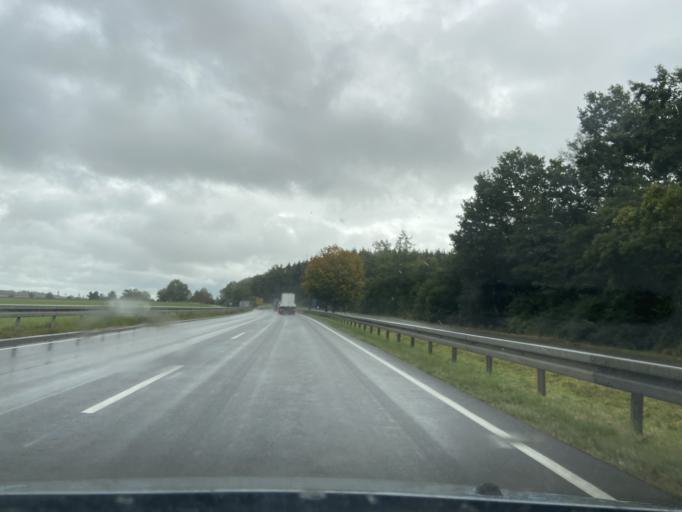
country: DE
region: Baden-Wuerttemberg
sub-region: Freiburg Region
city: Buchheim
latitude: 47.9870
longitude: 9.0234
